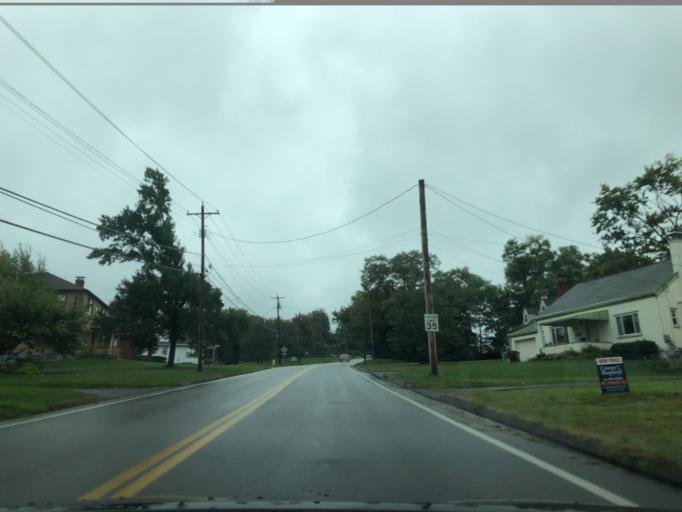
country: US
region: Ohio
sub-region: Hamilton County
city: Elmwood Place
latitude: 39.2046
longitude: -84.4984
